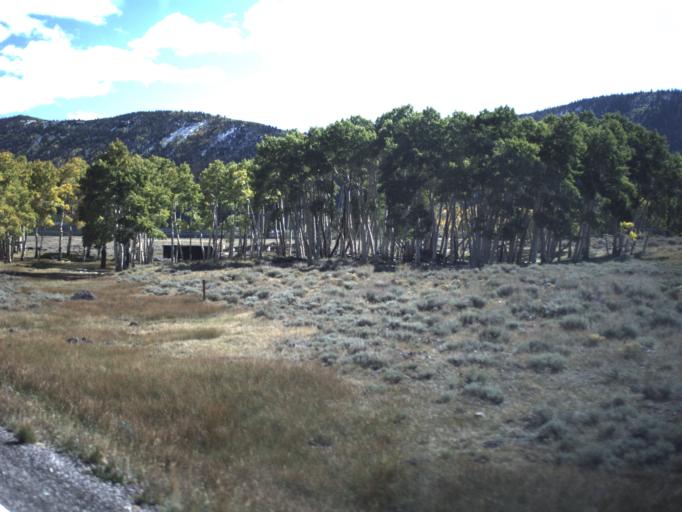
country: US
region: Utah
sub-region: Wayne County
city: Loa
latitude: 38.5305
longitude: -111.7425
